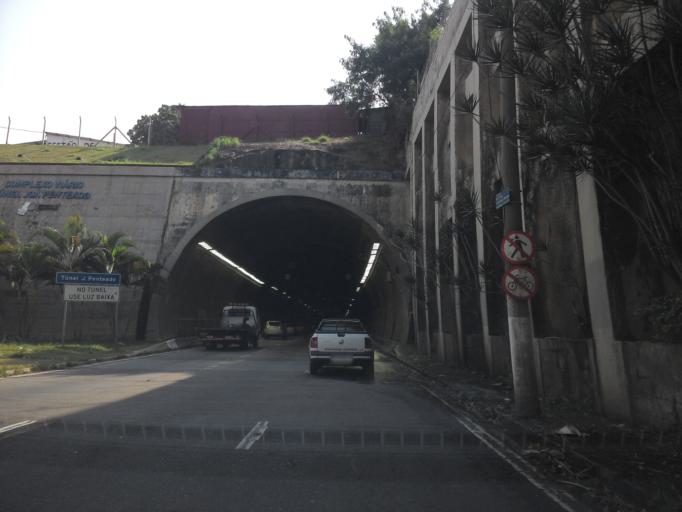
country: BR
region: Sao Paulo
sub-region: Campinas
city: Campinas
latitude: -22.9114
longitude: -47.0695
